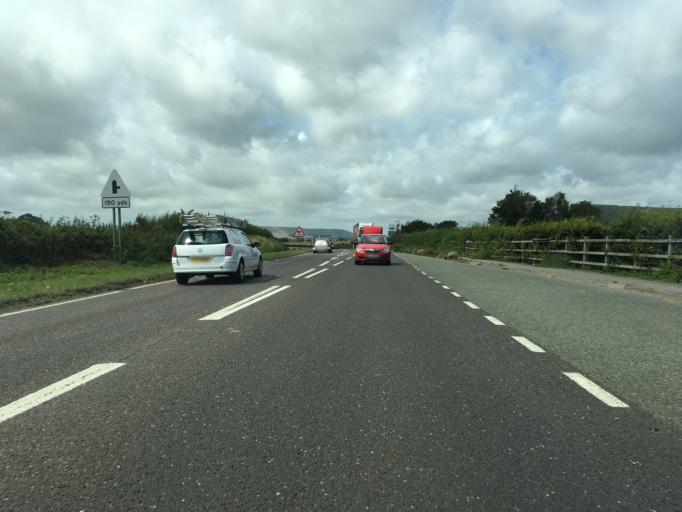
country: GB
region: England
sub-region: East Sussex
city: Ringmer
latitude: 50.8541
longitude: 0.0792
